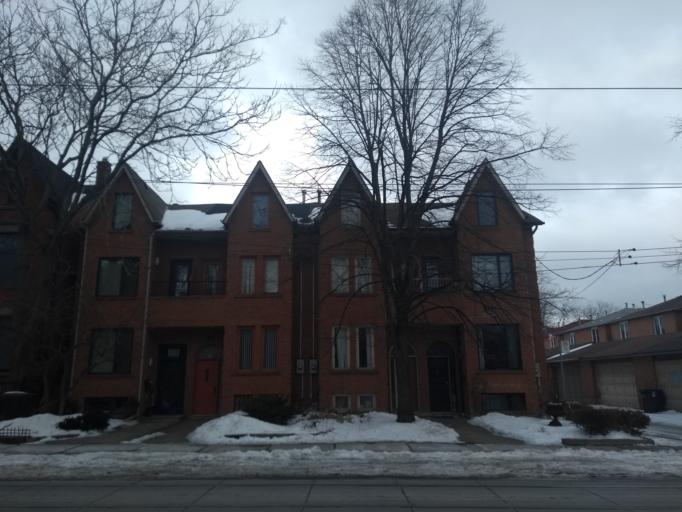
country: CA
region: Ontario
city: Toronto
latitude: 43.6432
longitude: -79.4158
